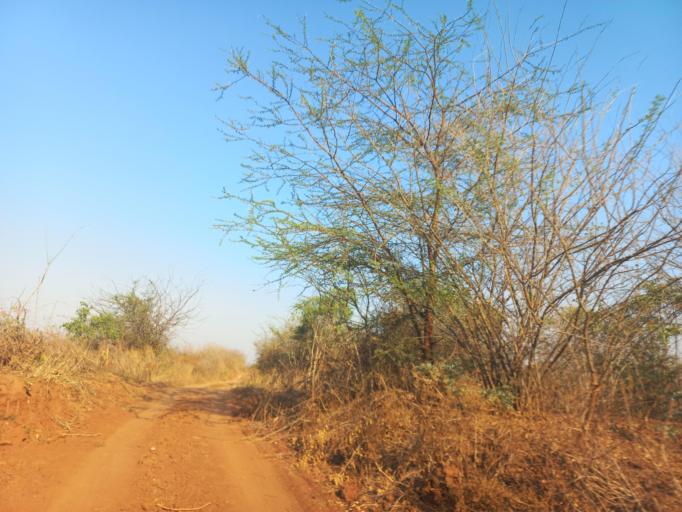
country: ZM
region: Lusaka
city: Luangwa
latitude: -15.4211
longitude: 30.2642
